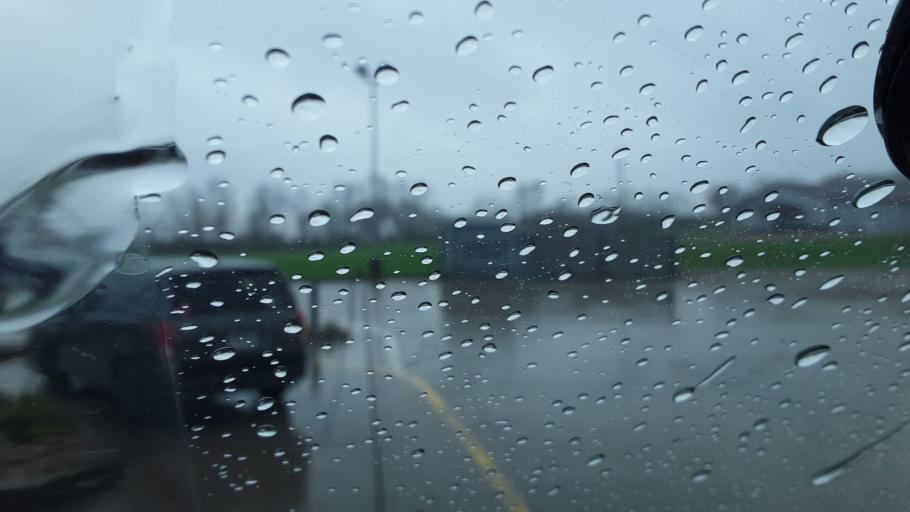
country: US
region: Ohio
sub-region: Vinton County
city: McArthur
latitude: 39.2527
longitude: -82.4918
